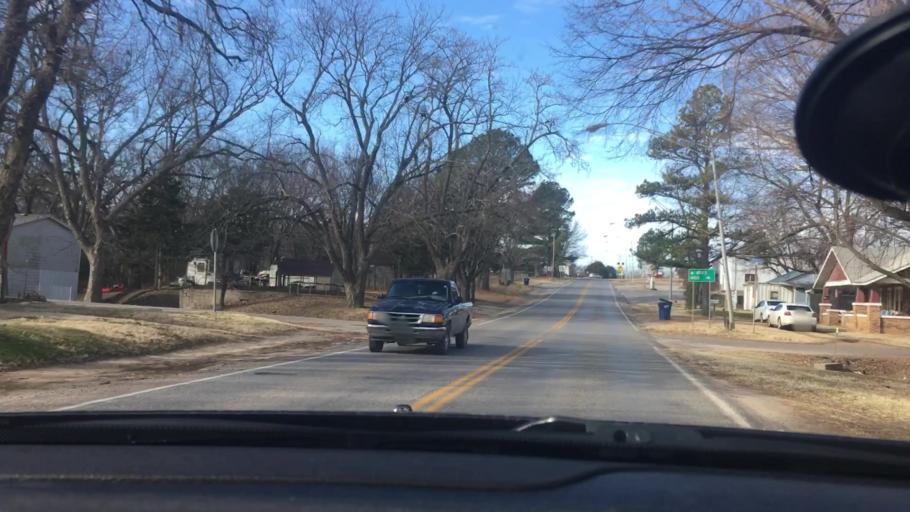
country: US
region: Oklahoma
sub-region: Seminole County
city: Konawa
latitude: 34.9602
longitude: -96.7557
